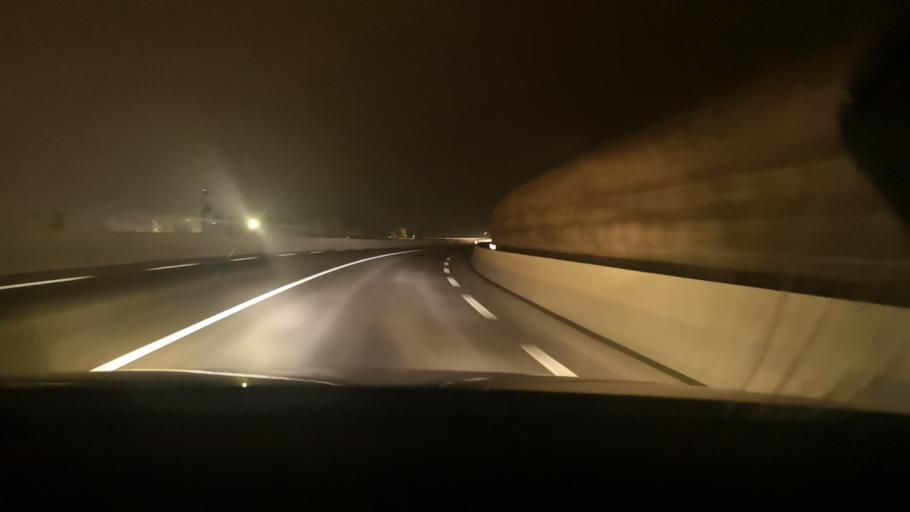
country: FR
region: Rhone-Alpes
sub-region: Departement de l'Ain
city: Montagnat
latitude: 46.1983
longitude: 5.2694
